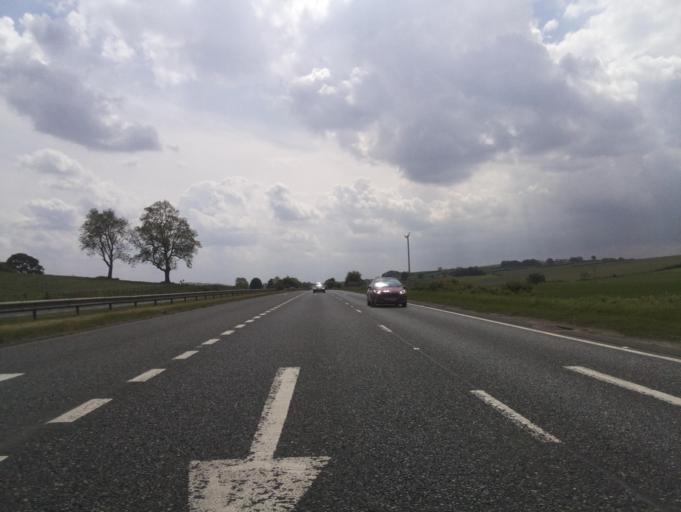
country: GB
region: England
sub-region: North Yorkshire
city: Northallerton
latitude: 54.3396
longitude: -1.3333
